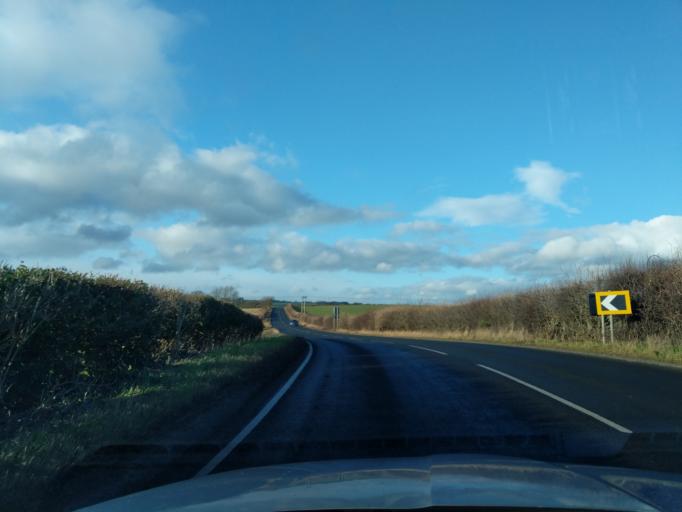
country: GB
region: England
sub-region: North Yorkshire
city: Catterick
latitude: 54.3148
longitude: -1.6736
